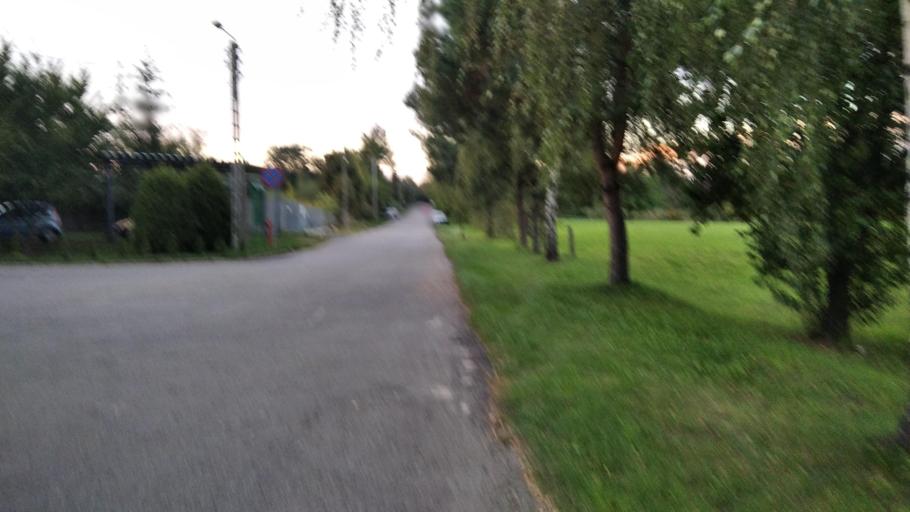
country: PL
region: Silesian Voivodeship
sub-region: Powiat bedzinski
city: Sarnow
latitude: 50.4034
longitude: 19.1381
